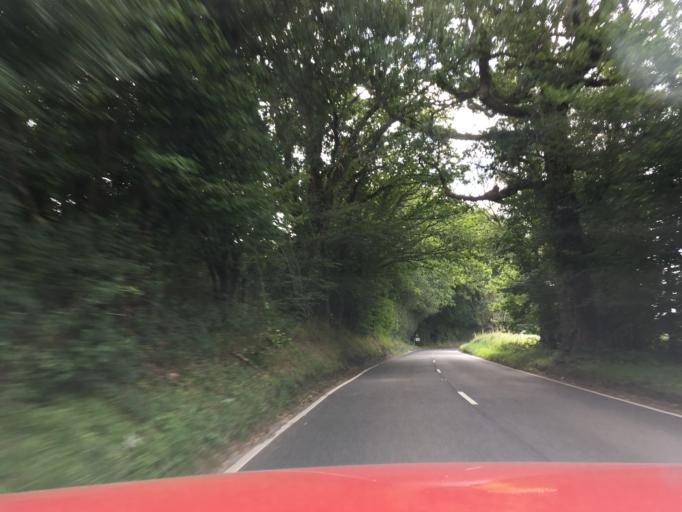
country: GB
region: England
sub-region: East Sussex
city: Crowborough
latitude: 51.1050
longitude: 0.1499
